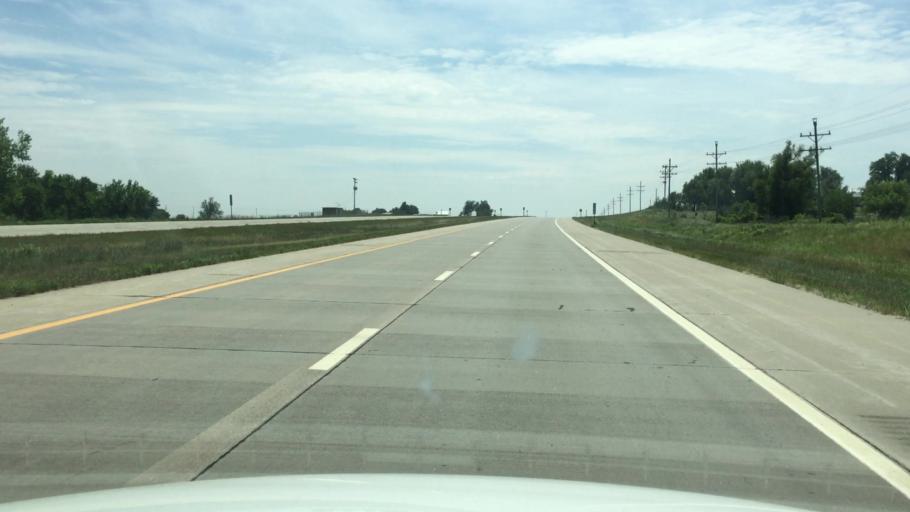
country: US
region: Kansas
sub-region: Jackson County
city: Holton
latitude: 39.2828
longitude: -95.7194
